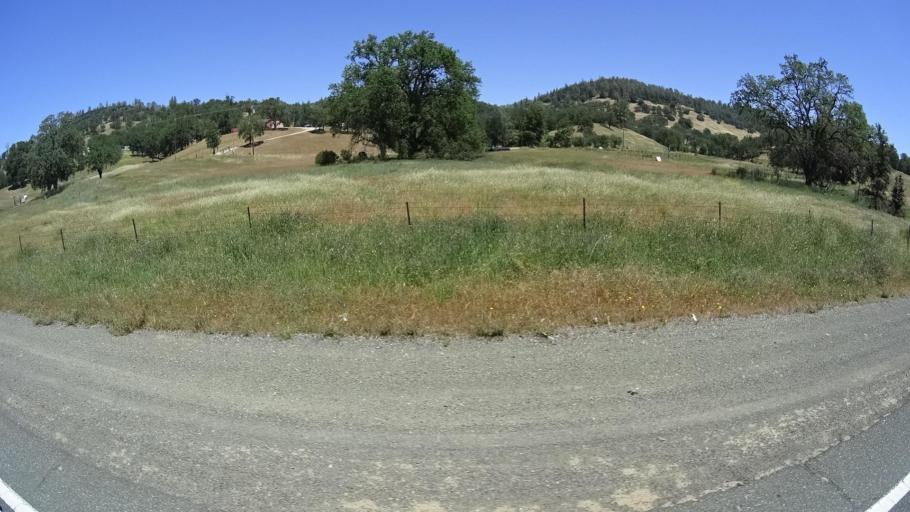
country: US
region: California
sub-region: Lake County
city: Lower Lake
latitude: 38.8469
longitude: -122.6101
